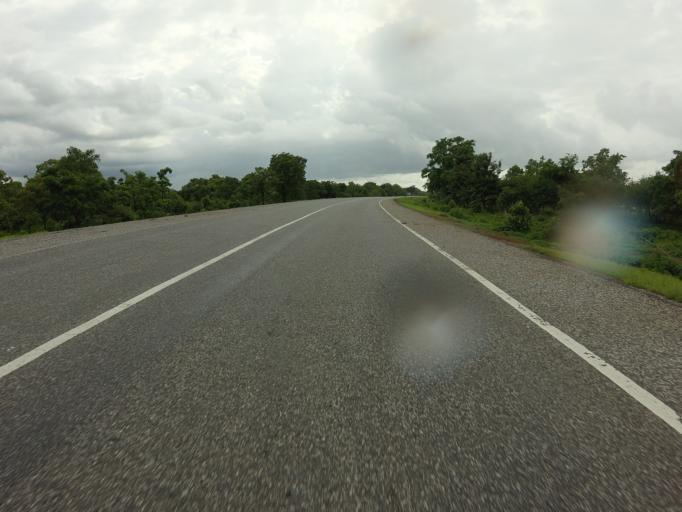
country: GH
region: Northern
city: Tamale
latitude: 9.1367
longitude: -1.3451
